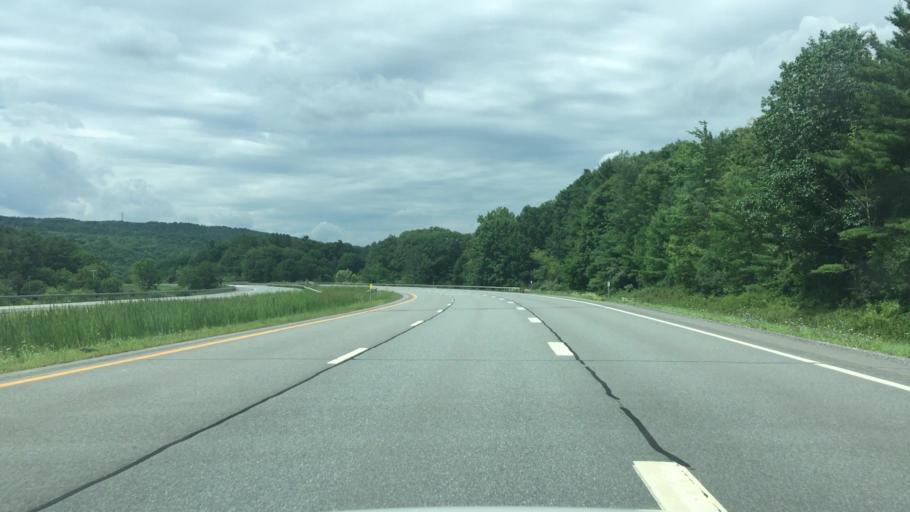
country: US
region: New York
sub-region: Schenectady County
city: Rotterdam
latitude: 42.7797
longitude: -74.0437
